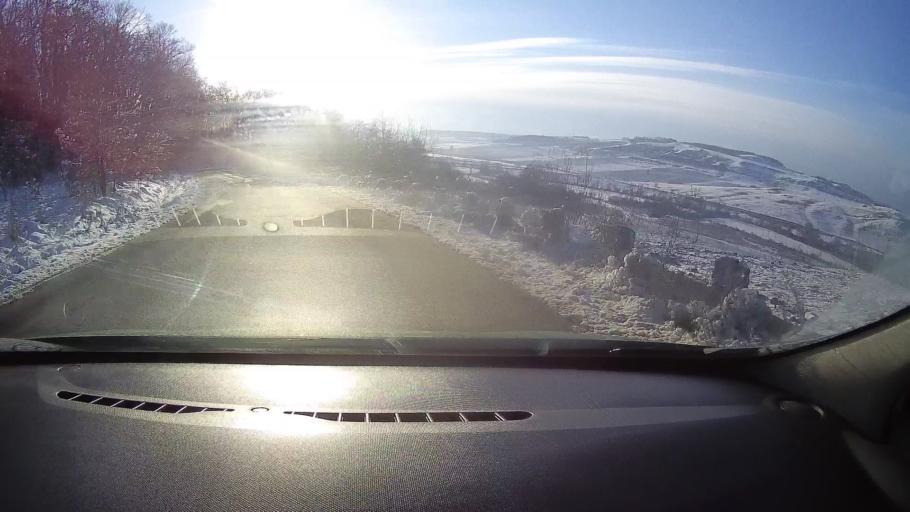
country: RO
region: Sibiu
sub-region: Oras Agnita
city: Ruja
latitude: 45.9890
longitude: 24.6704
